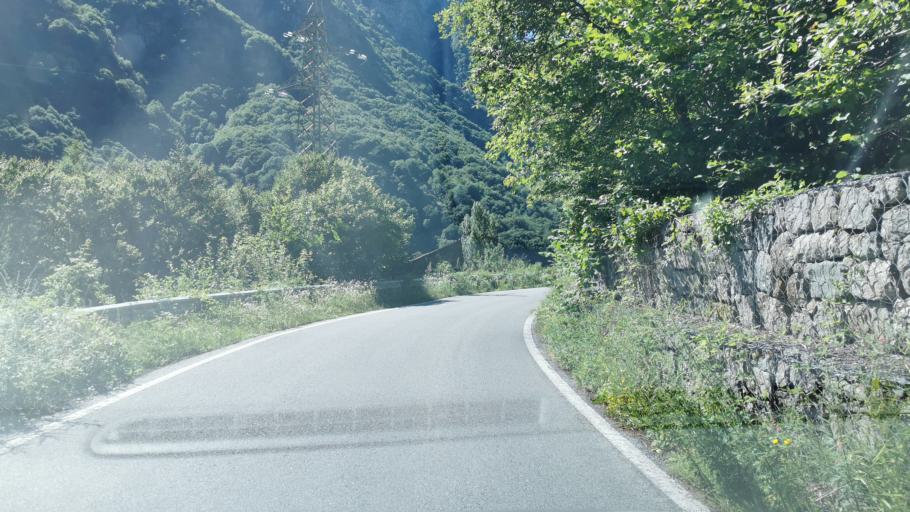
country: IT
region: Piedmont
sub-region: Provincia di Cuneo
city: Entracque
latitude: 44.2201
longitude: 7.3864
